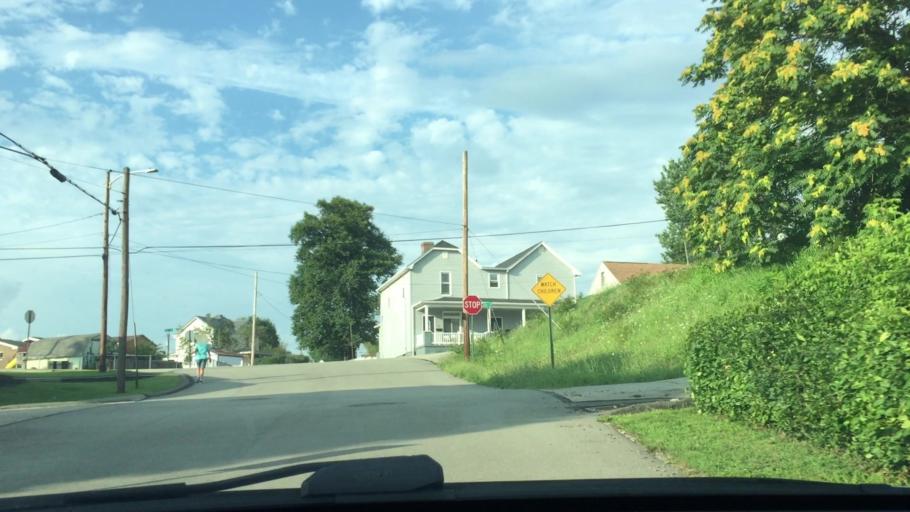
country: US
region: Pennsylvania
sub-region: Fayette County
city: Belle Vernon
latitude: 40.1289
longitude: -79.8618
